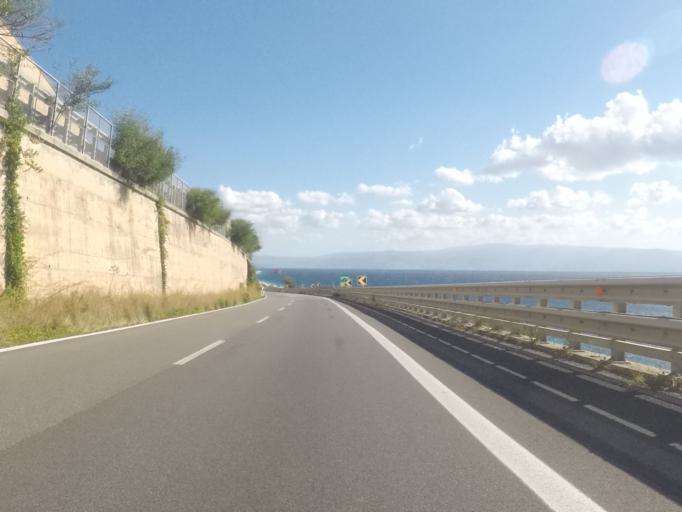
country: IT
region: Sicily
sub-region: Messina
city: Itala
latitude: 38.0301
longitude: 15.4449
